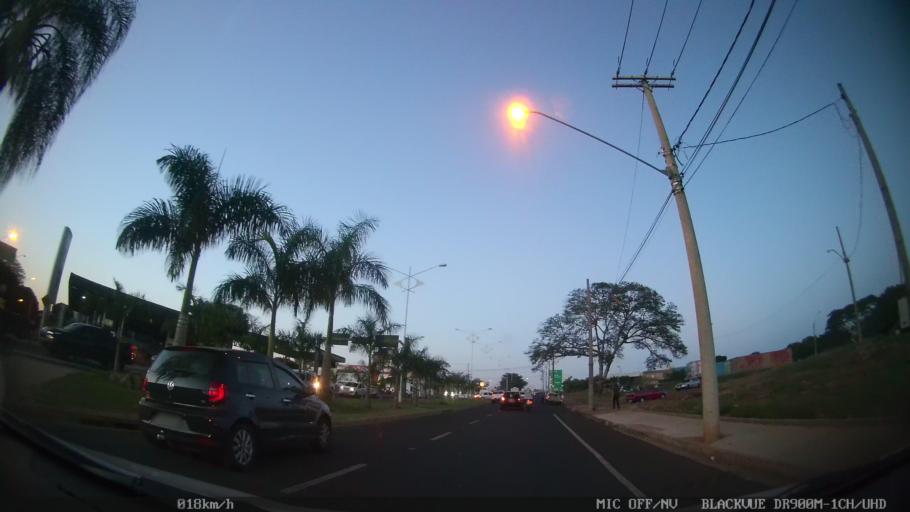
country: BR
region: Sao Paulo
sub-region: Sao Jose Do Rio Preto
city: Sao Jose do Rio Preto
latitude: -20.8031
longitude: -49.3592
